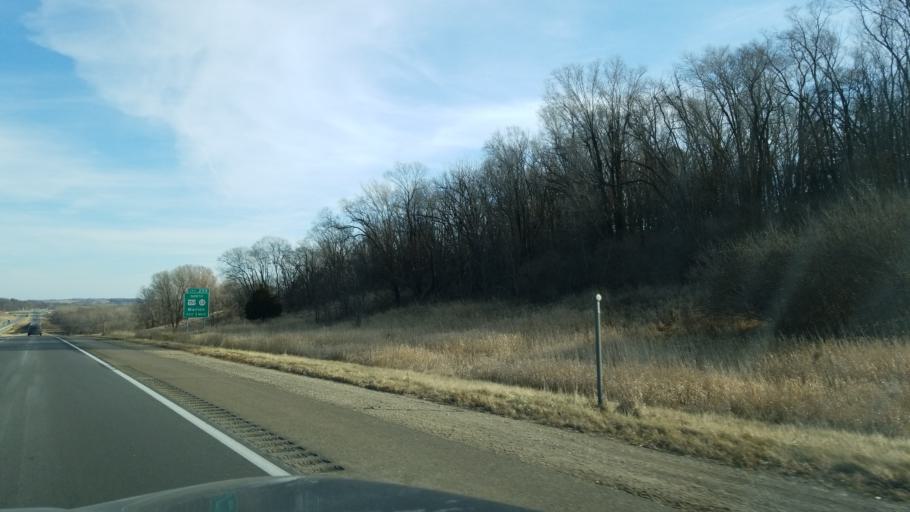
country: US
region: Iowa
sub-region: Linn County
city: Ely
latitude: 41.9254
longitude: -91.5618
